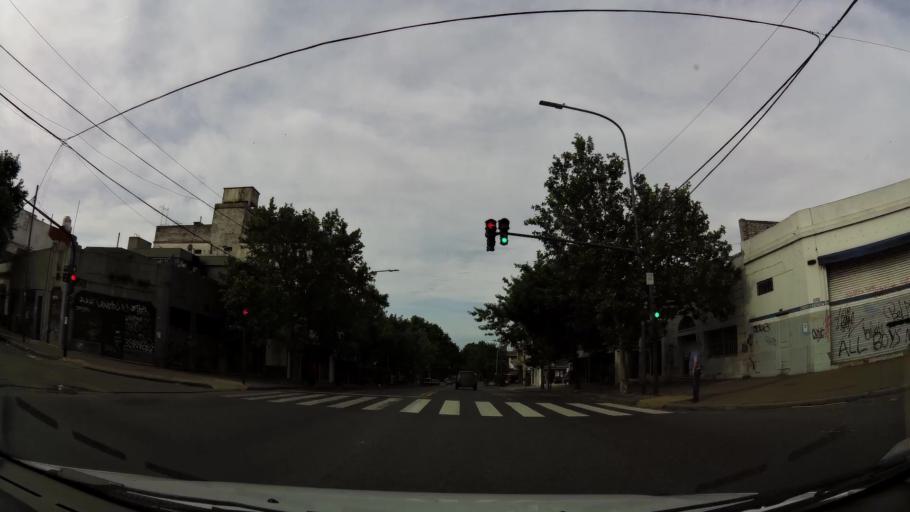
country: AR
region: Buenos Aires F.D.
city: Villa Lugano
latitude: -34.6484
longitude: -58.4687
